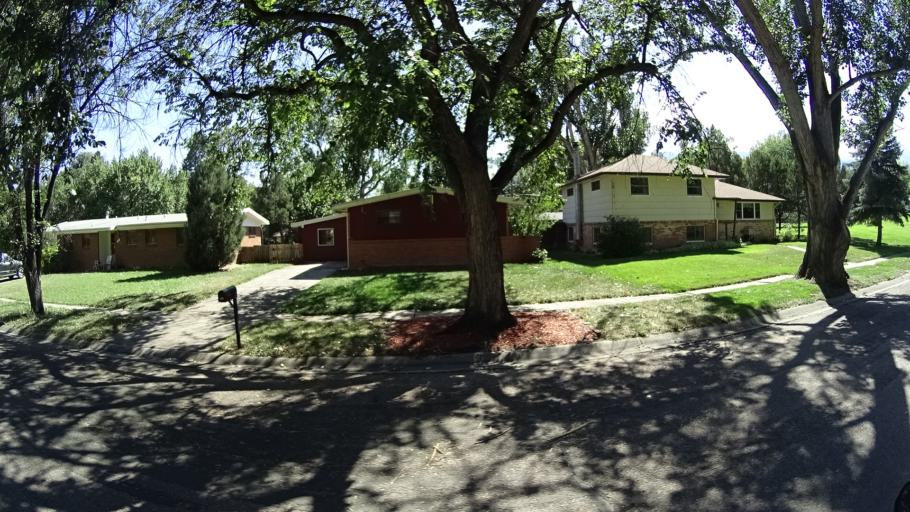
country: US
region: Colorado
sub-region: El Paso County
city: Manitou Springs
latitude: 38.8631
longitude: -104.8697
